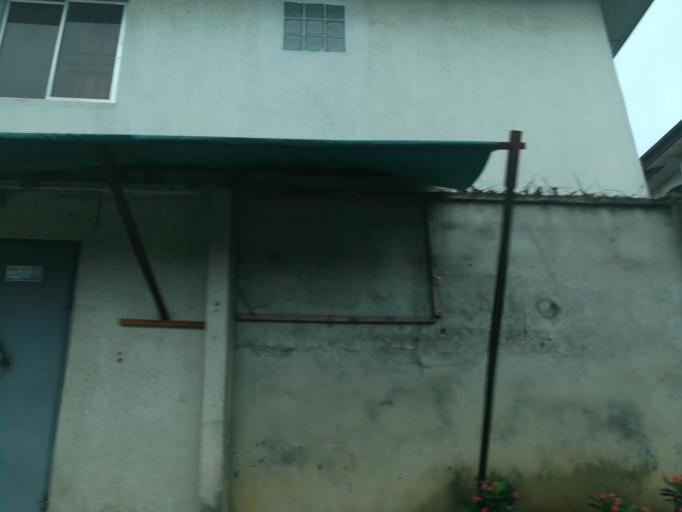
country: NG
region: Rivers
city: Port Harcourt
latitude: 4.8612
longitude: 7.0370
